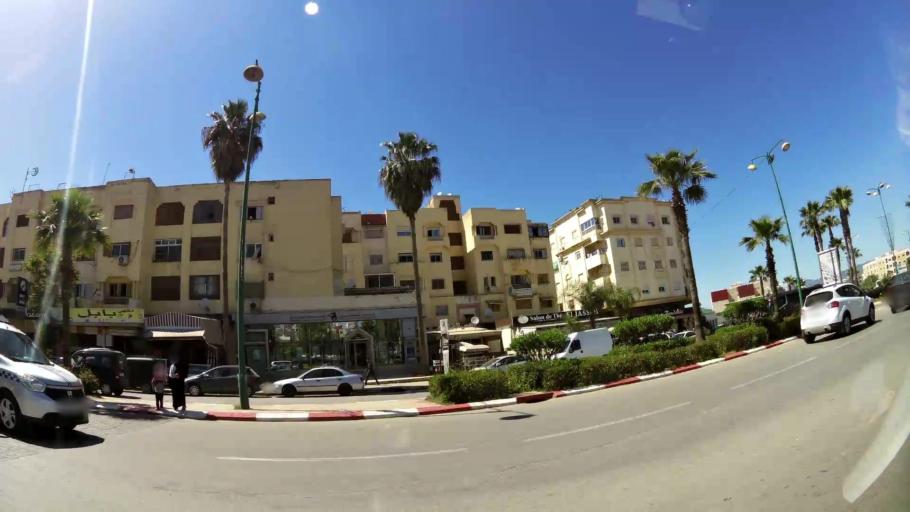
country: MA
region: Meknes-Tafilalet
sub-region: Meknes
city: Meknes
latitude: 33.8917
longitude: -5.5758
